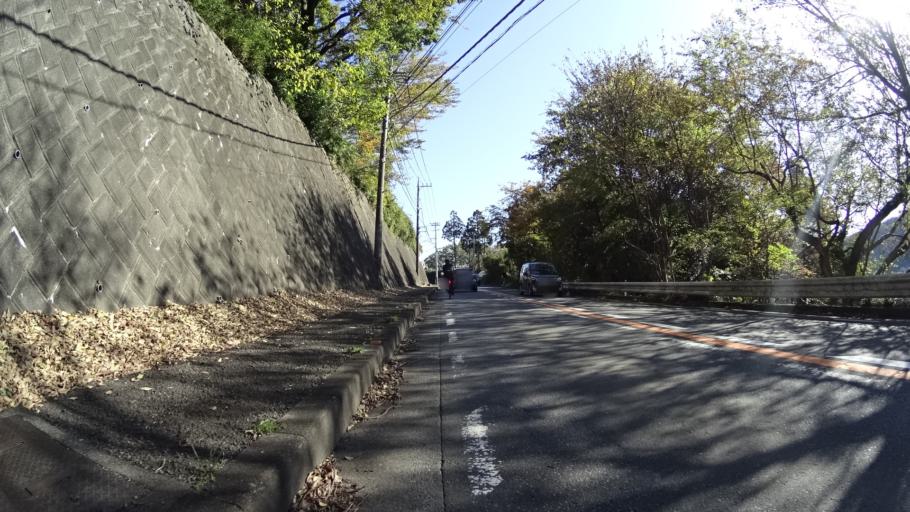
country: JP
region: Kanagawa
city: Zama
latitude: 35.5297
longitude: 139.3145
